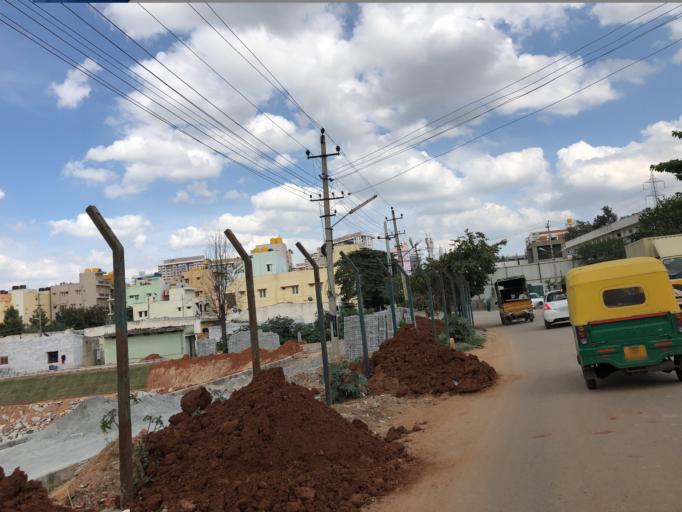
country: IN
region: Karnataka
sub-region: Bangalore Urban
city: Bangalore
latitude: 12.9902
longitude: 77.6960
